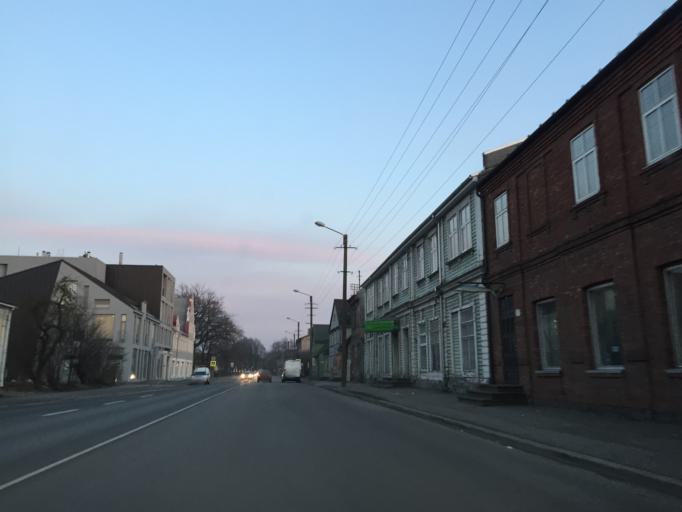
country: EE
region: Paernumaa
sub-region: Paernu linn
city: Parnu
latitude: 58.3848
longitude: 24.5142
